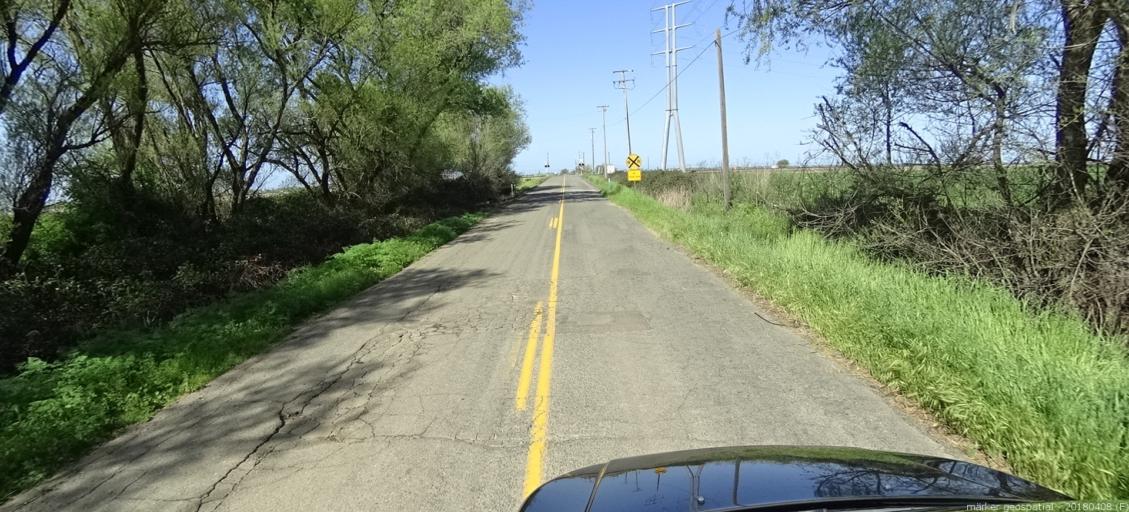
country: US
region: California
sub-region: Sacramento County
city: Laguna
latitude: 38.3574
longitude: -121.4469
